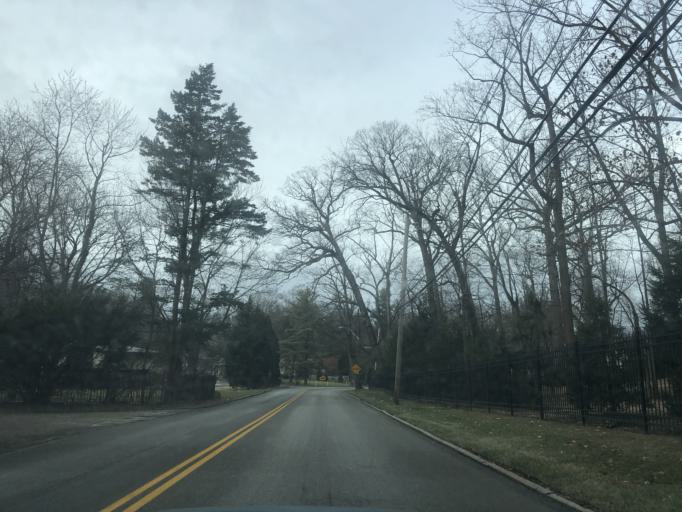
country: US
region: Pennsylvania
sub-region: Delaware County
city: Radnor
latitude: 40.0457
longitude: -75.3357
